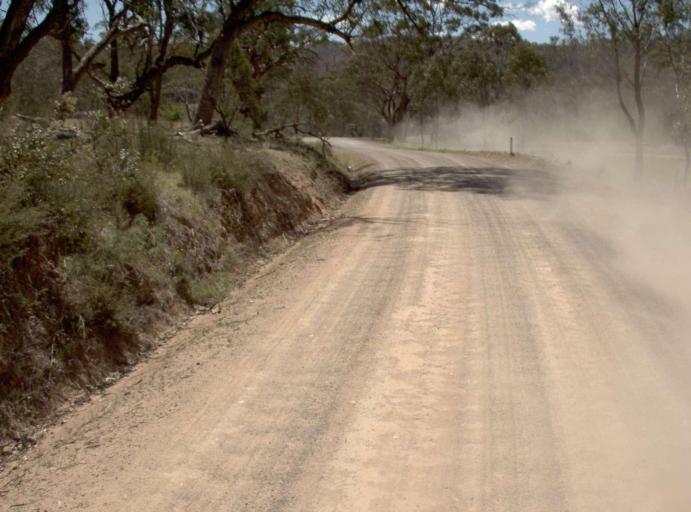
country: AU
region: New South Wales
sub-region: Snowy River
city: Jindabyne
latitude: -37.0407
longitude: 148.5587
